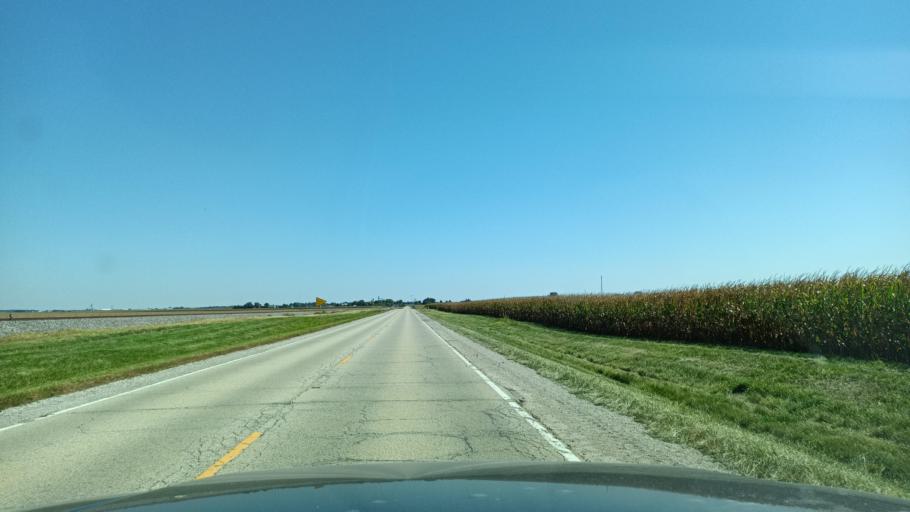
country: US
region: Illinois
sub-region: Tazewell County
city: Mackinaw
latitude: 40.6267
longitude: -89.3191
